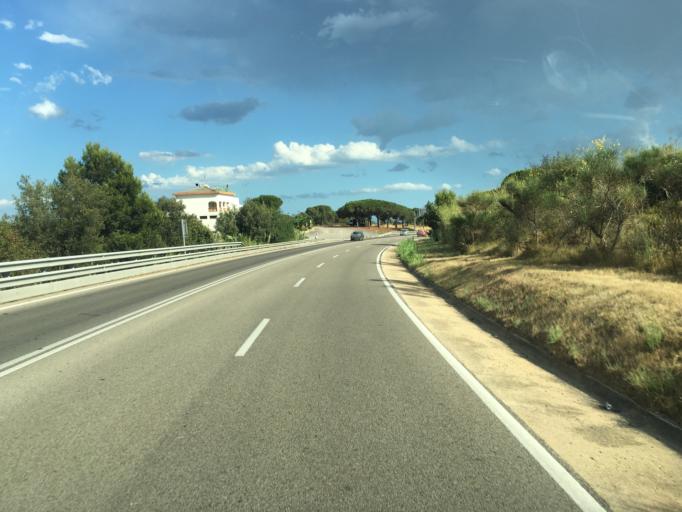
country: ES
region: Catalonia
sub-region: Provincia de Barcelona
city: Palafolls
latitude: 41.6666
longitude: 2.7306
